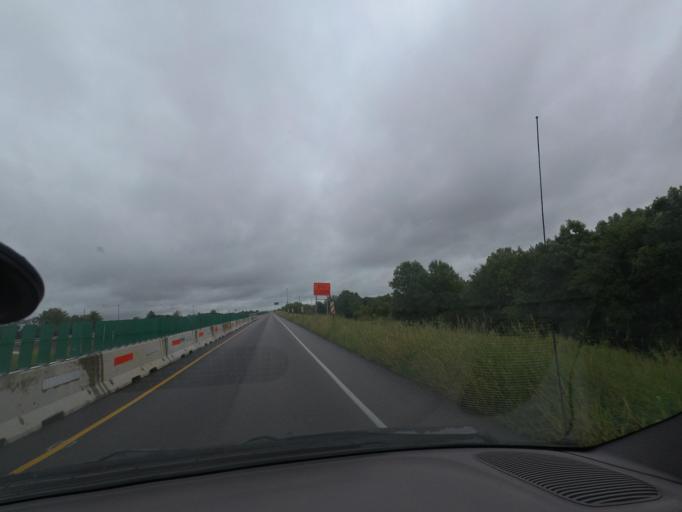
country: US
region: Illinois
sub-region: Piatt County
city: Cerro Gordo
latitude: 39.9879
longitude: -88.7865
